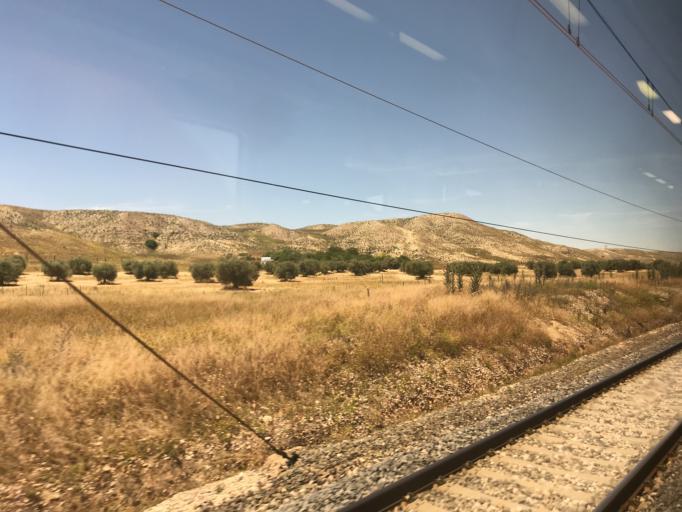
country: ES
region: Madrid
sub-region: Provincia de Madrid
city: Ciempozuelos
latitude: 40.1280
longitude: -3.6161
